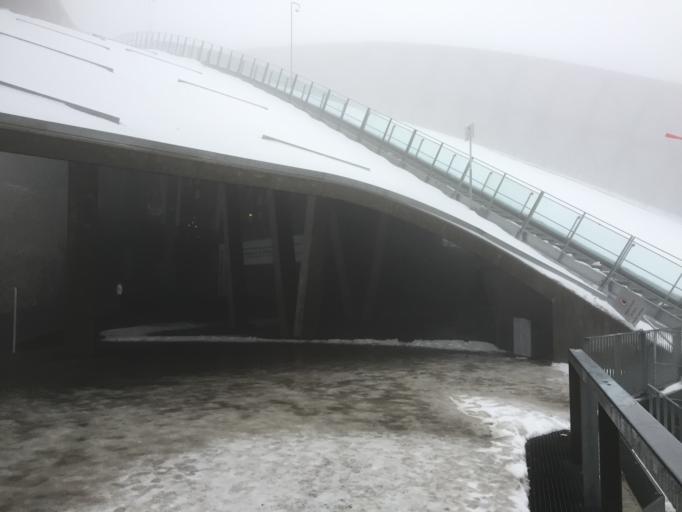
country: NO
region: Oslo
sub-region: Oslo
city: Sjolyststranda
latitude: 59.9641
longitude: 10.6670
